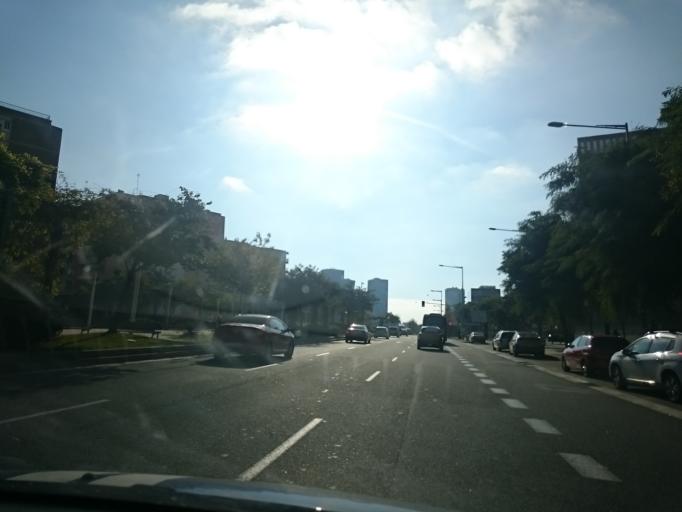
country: ES
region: Catalonia
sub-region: Provincia de Barcelona
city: Sants-Montjuic
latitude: 41.3635
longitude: 2.1334
